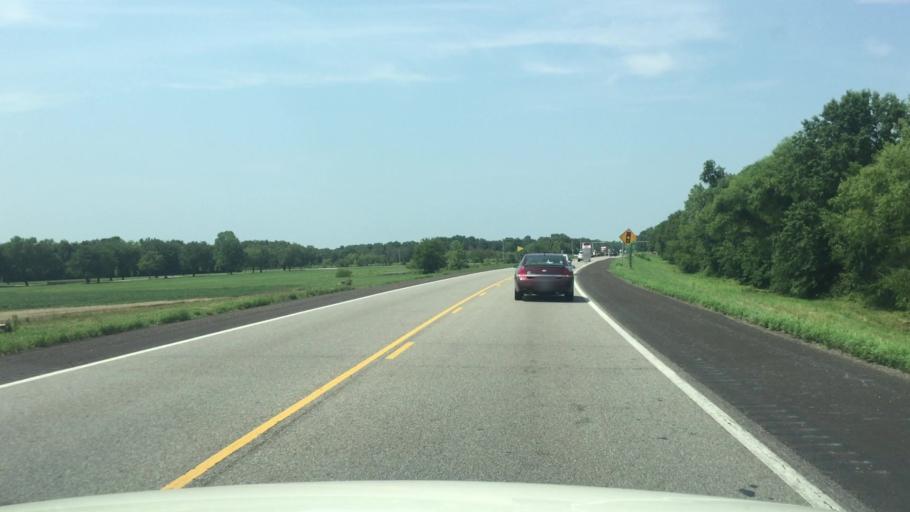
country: US
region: Kansas
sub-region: Crawford County
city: Pittsburg
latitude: 37.3927
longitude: -94.7170
